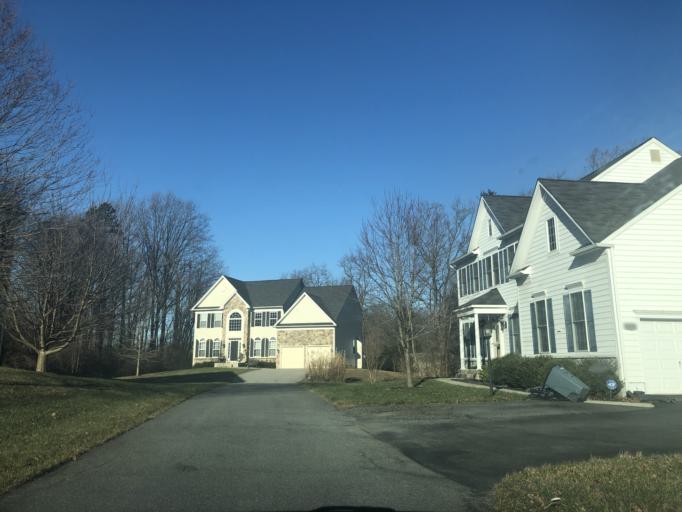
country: US
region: Maryland
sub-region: Howard County
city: Columbia
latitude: 39.2034
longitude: -76.8468
